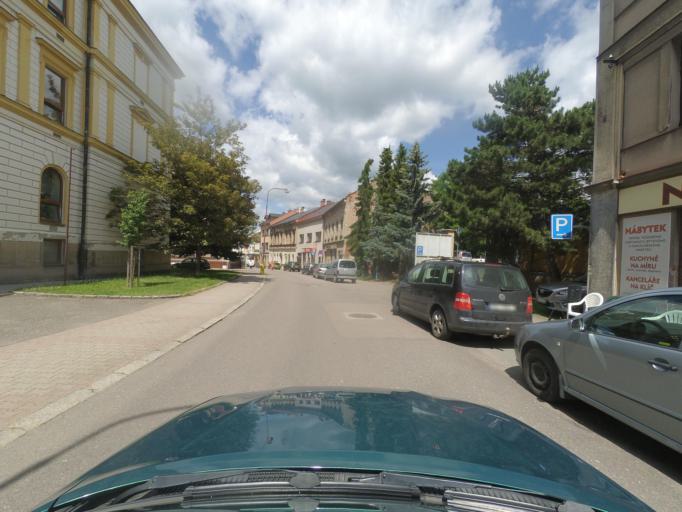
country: CZ
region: Pardubicky
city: Zamberk
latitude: 50.0854
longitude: 16.4652
